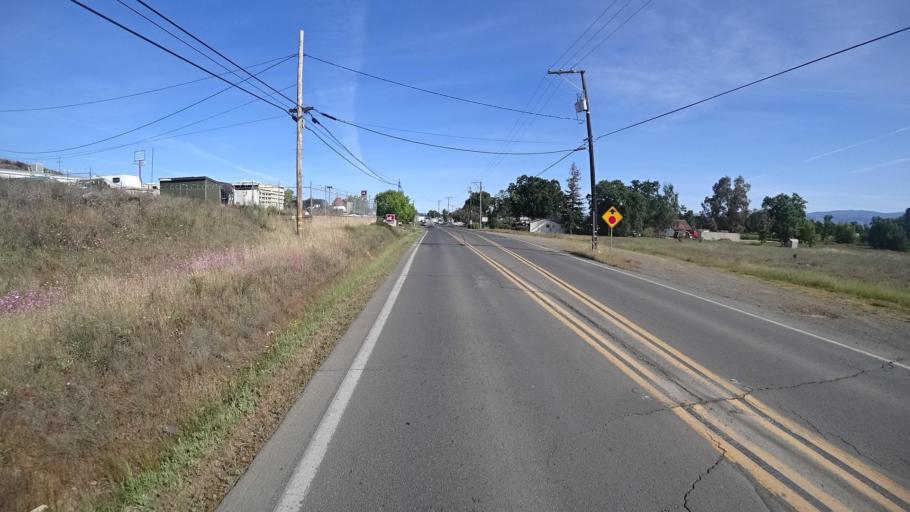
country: US
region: California
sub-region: Lake County
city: Lakeport
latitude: 39.0159
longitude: -122.9110
